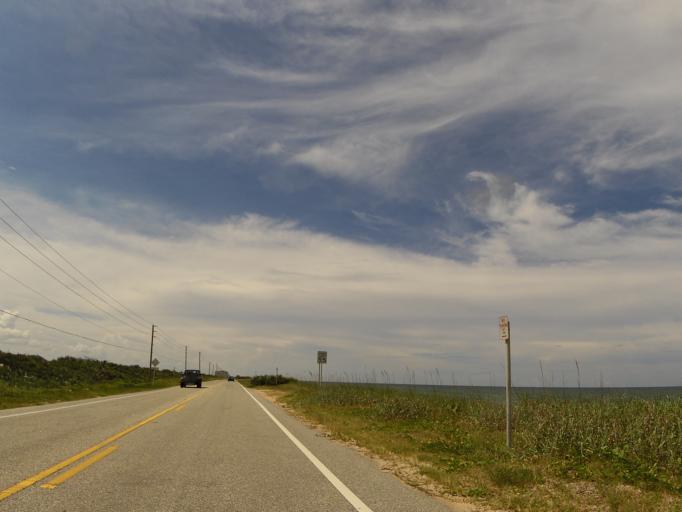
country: US
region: Florida
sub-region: Volusia County
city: Ormond-by-the-Sea
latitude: 29.4111
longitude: -81.0952
